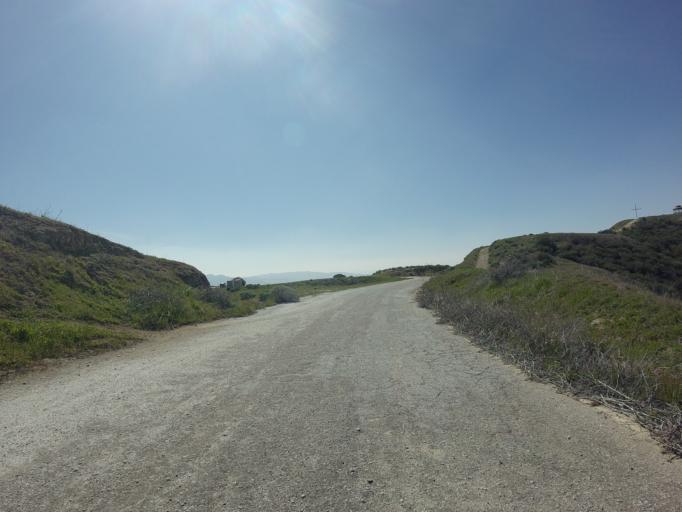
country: US
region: California
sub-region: Riverside County
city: Beaumont
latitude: 33.9163
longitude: -117.0535
